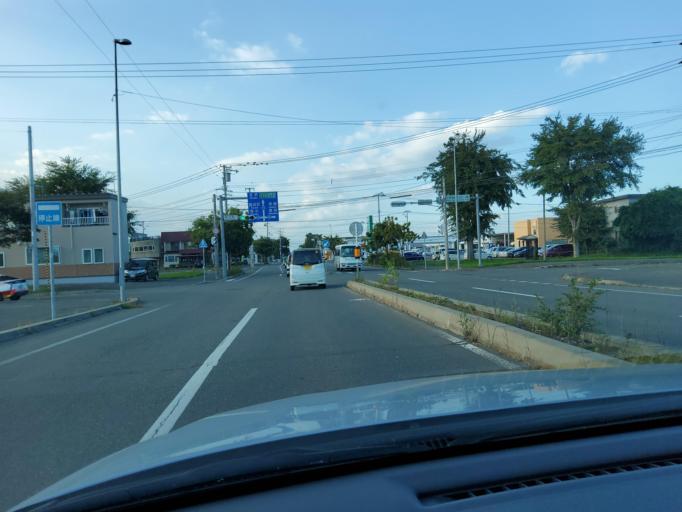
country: JP
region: Hokkaido
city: Obihiro
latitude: 42.9292
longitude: 143.1852
